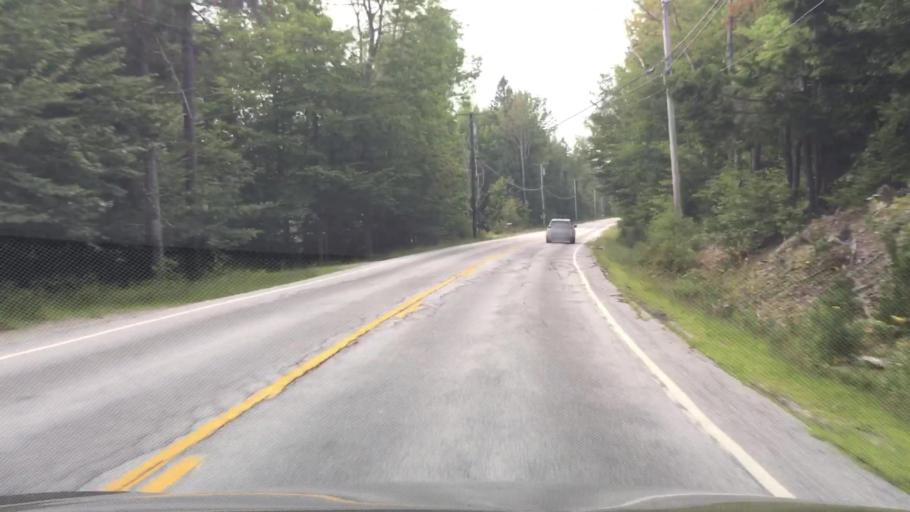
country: US
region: Maine
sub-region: Hancock County
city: Penobscot
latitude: 44.4284
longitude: -68.6037
